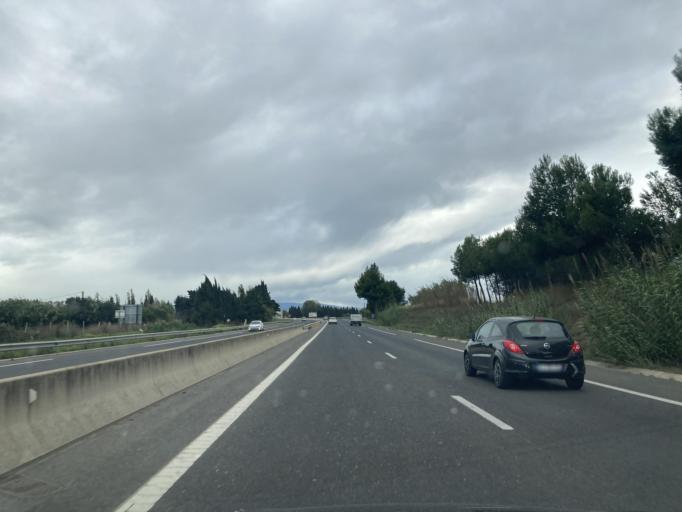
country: FR
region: Languedoc-Roussillon
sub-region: Departement des Pyrenees-Orientales
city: Elne
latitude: 42.6169
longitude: 2.9690
